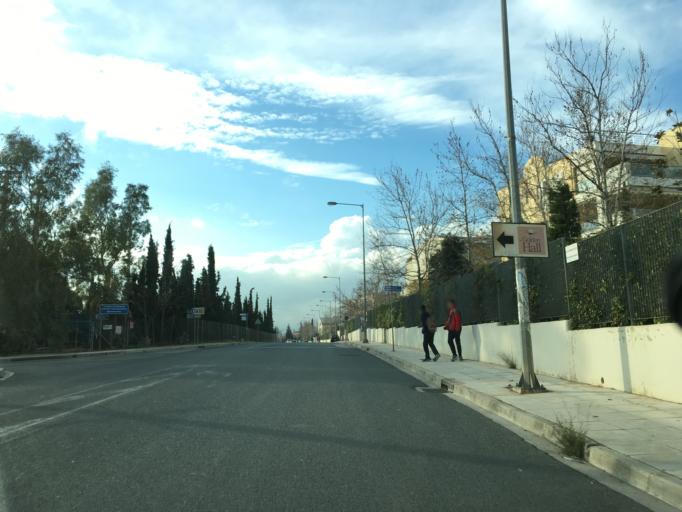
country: GR
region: Attica
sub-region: Nomarchia Athinas
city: Marousi
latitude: 38.0403
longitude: 23.7935
